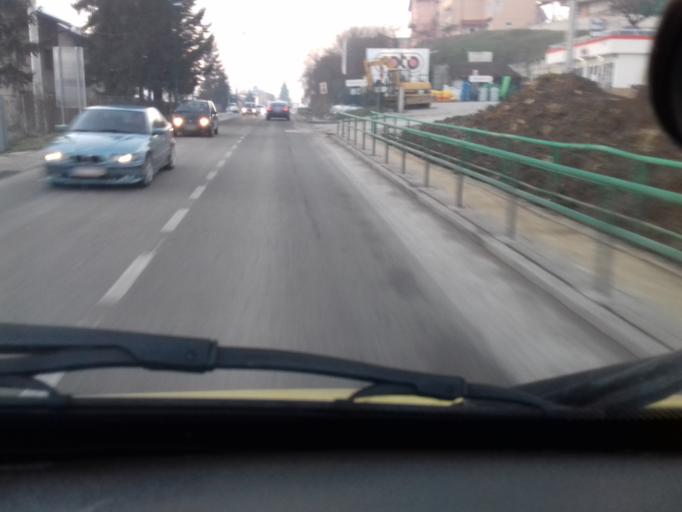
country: BA
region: Federation of Bosnia and Herzegovina
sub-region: Kanton Sarajevo
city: Sarajevo
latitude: 43.8560
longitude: 18.3244
